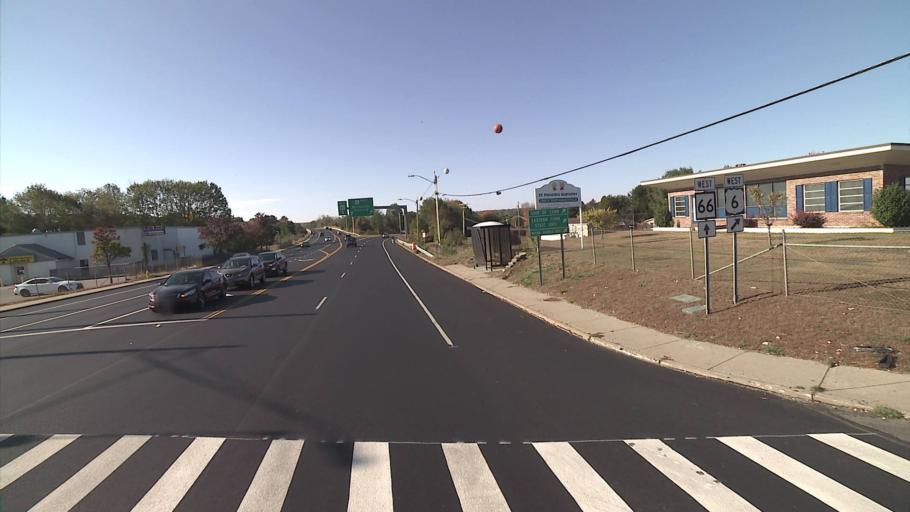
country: US
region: Connecticut
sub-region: Windham County
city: Willimantic
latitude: 41.7376
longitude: -72.1810
